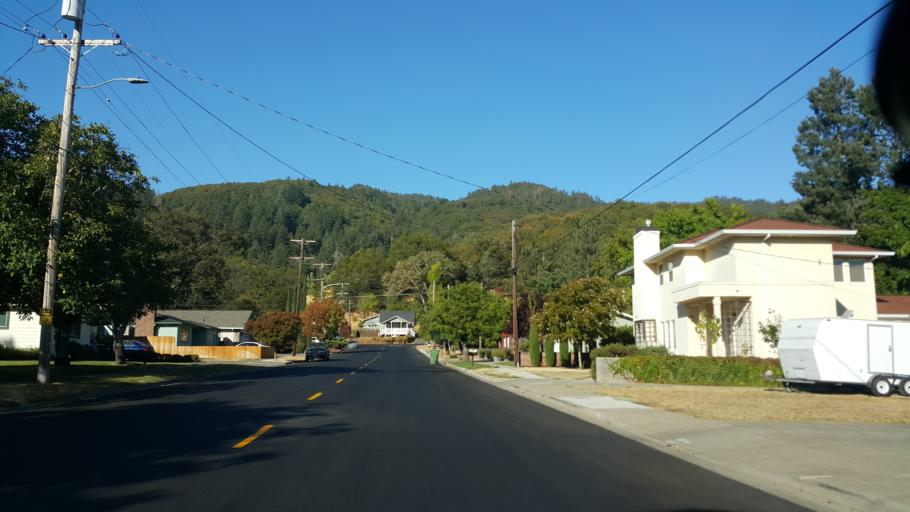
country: US
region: California
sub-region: Mendocino County
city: Ukiah
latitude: 39.1368
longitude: -123.2127
